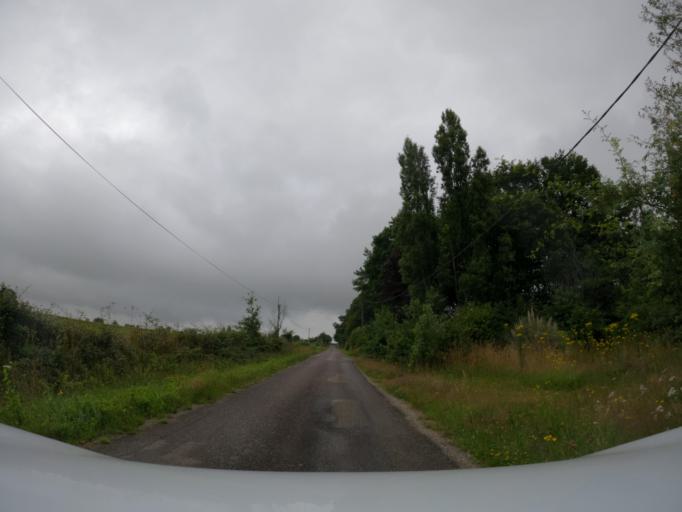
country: FR
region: Pays de la Loire
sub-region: Departement de la Loire-Atlantique
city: Saint-Mars-du-Desert
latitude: 47.3847
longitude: -1.4088
